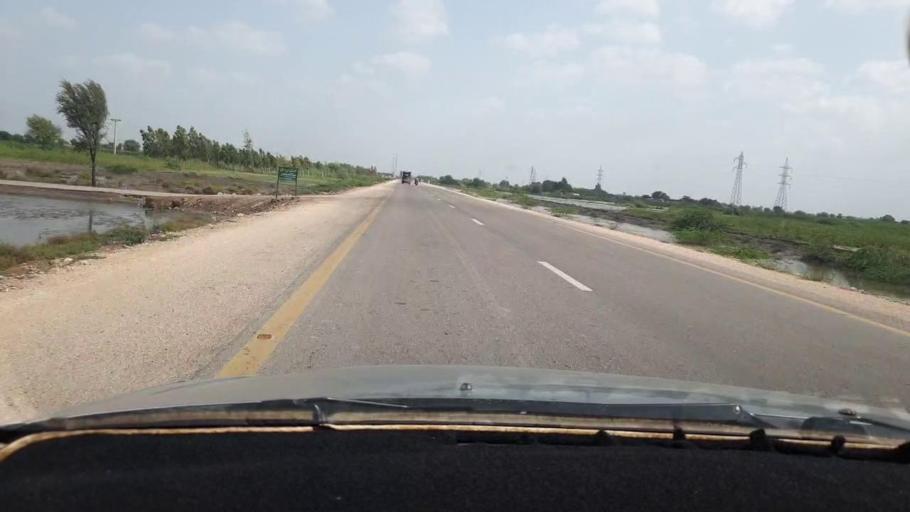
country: PK
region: Sindh
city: Digri
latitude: 25.0376
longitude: 69.2380
